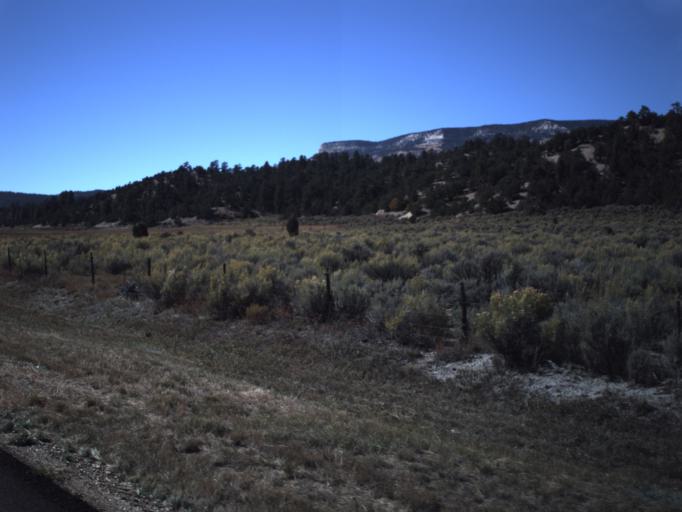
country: US
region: Utah
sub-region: Garfield County
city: Panguitch
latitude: 37.6926
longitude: -111.7989
